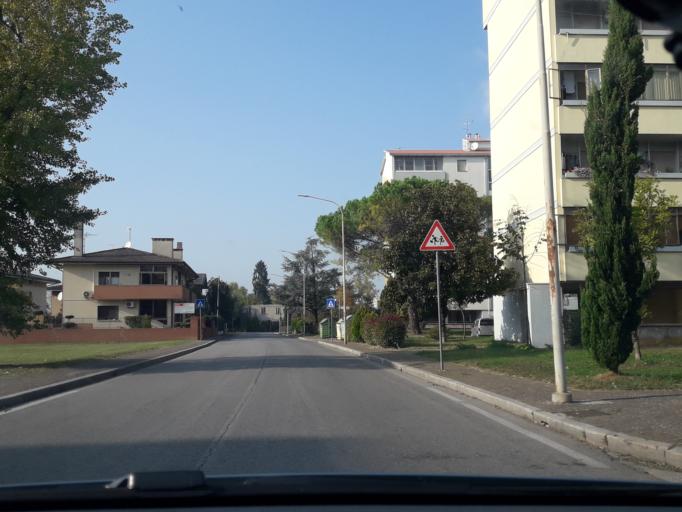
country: IT
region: Friuli Venezia Giulia
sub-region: Provincia di Udine
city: Udine
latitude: 46.0787
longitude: 13.2605
